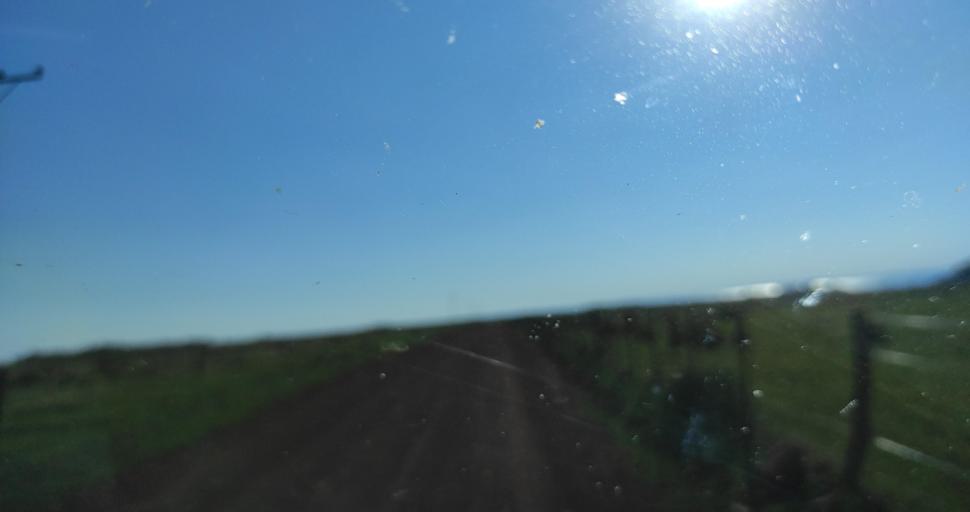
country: PY
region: Itapua
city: Carmen del Parana
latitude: -27.4092
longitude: -56.1577
